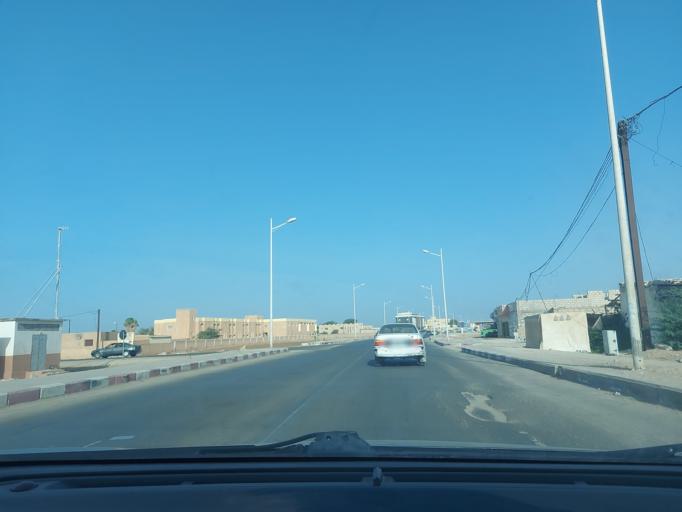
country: MR
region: Nouakchott
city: Nouakchott
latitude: 18.0841
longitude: -15.9973
